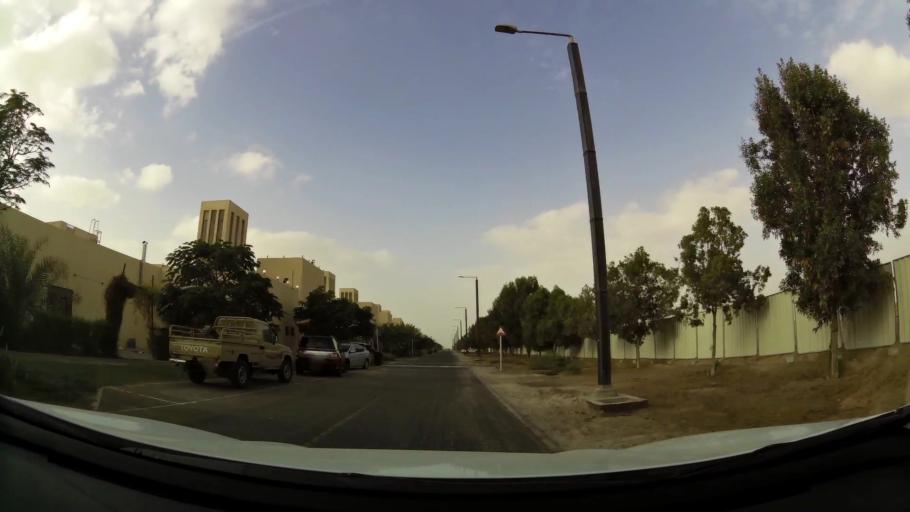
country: AE
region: Abu Dhabi
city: Abu Dhabi
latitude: 24.5077
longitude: 54.6022
